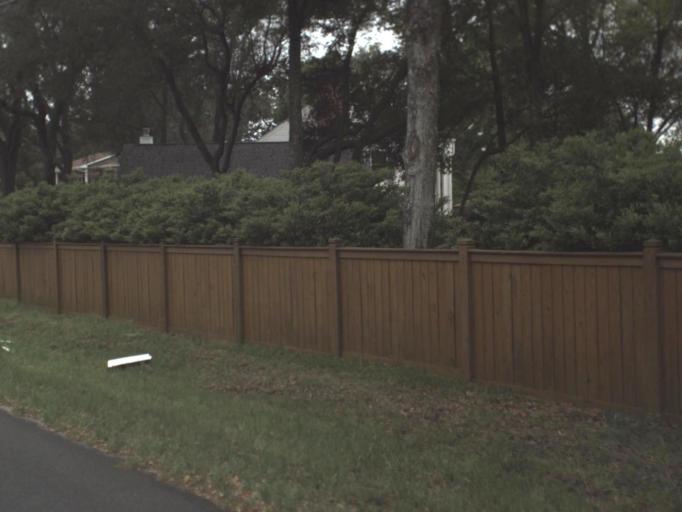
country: US
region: Florida
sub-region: Escambia County
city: East Pensacola Heights
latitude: 30.4427
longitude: -87.1737
